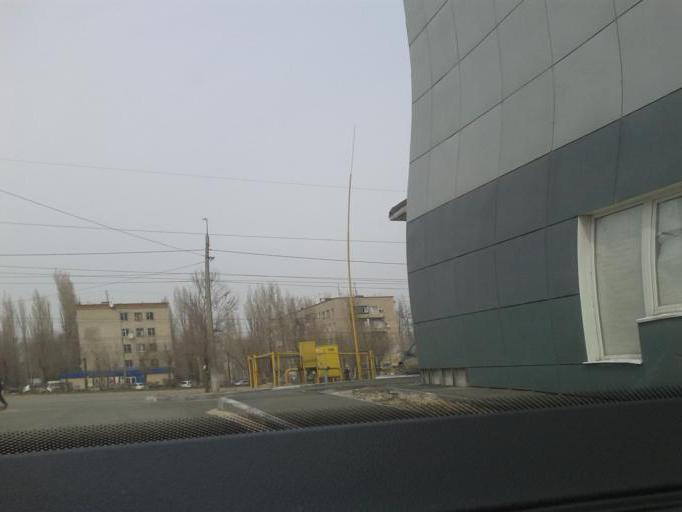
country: RU
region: Volgograd
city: Gorodishche
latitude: 48.7669
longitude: 44.4900
